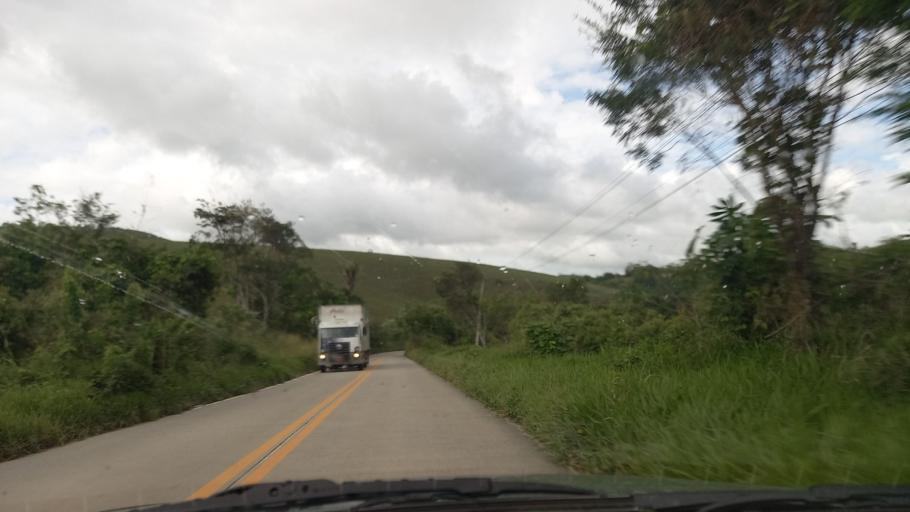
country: BR
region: Pernambuco
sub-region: Quipapa
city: Quipapa
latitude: -8.7914
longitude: -35.9843
